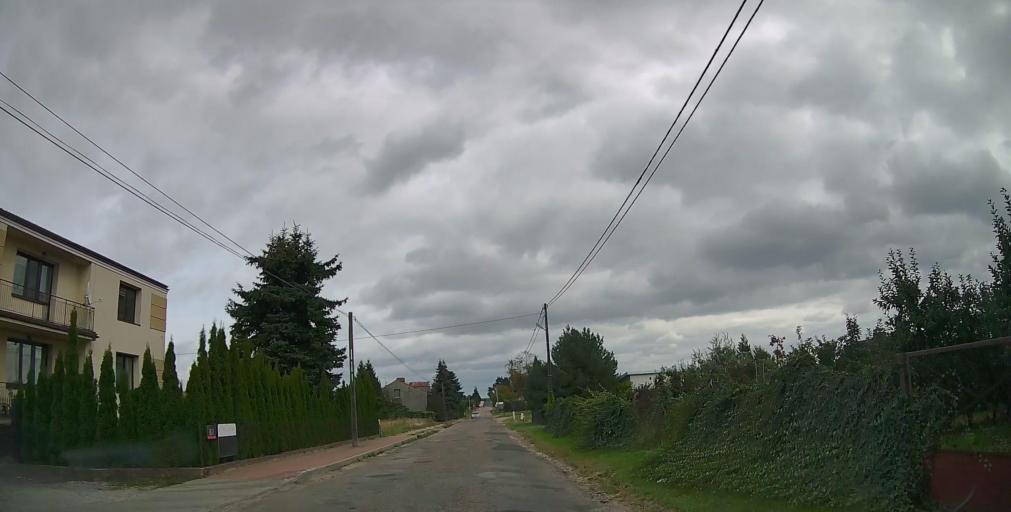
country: PL
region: Masovian Voivodeship
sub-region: Powiat grojecki
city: Belsk Duzy
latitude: 51.8166
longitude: 20.8263
